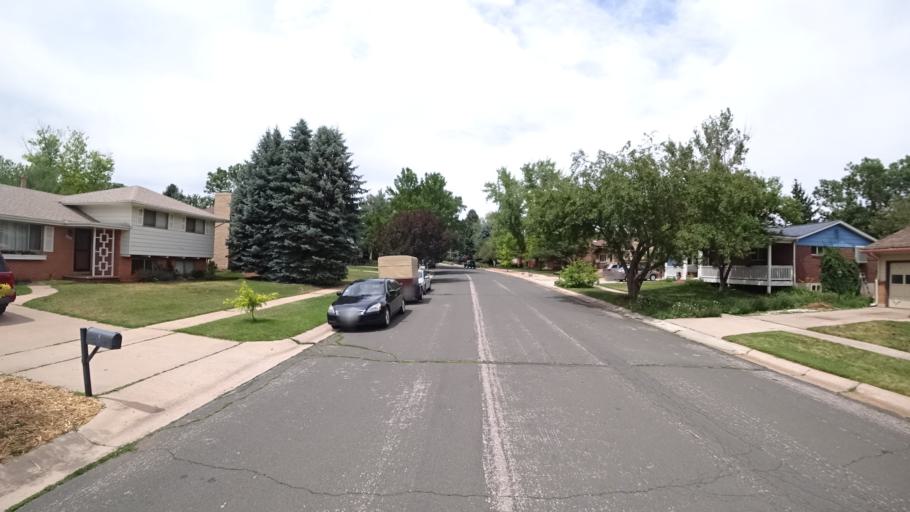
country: US
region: Colorado
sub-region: El Paso County
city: Manitou Springs
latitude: 38.8679
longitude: -104.8705
